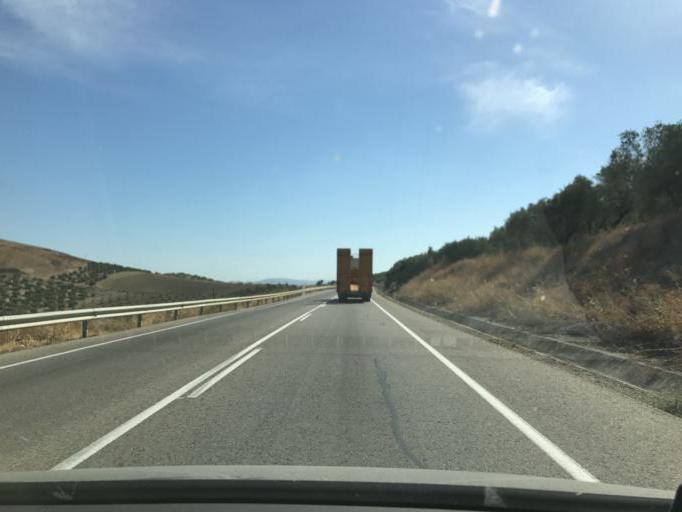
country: ES
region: Andalusia
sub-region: Province of Cordoba
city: Espejo
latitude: 37.6861
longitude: -4.5388
